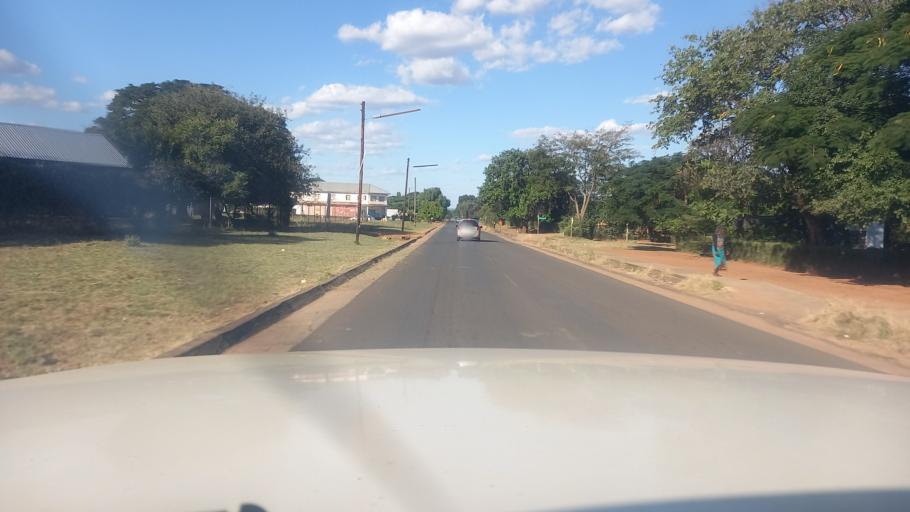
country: ZM
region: Southern
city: Livingstone
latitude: -17.8392
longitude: 25.8650
